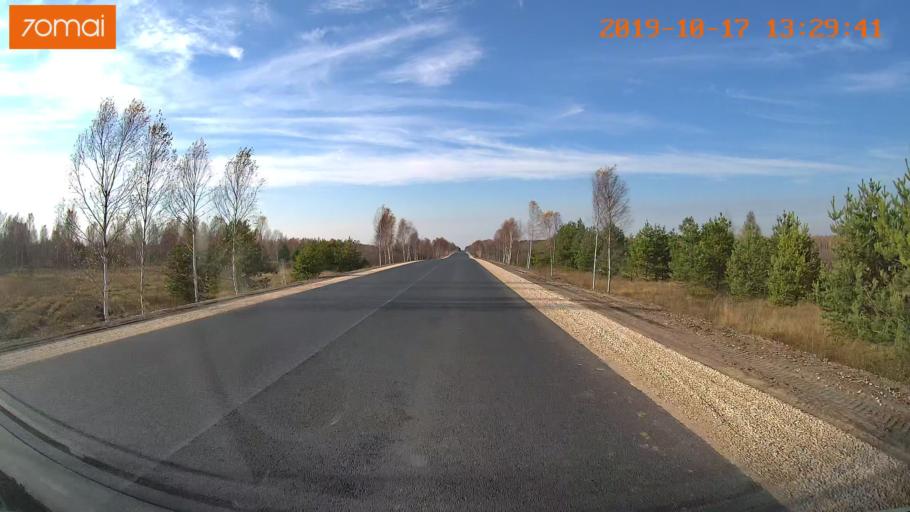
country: RU
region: Vladimir
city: Velikodvorskiy
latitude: 55.1206
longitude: 40.8350
